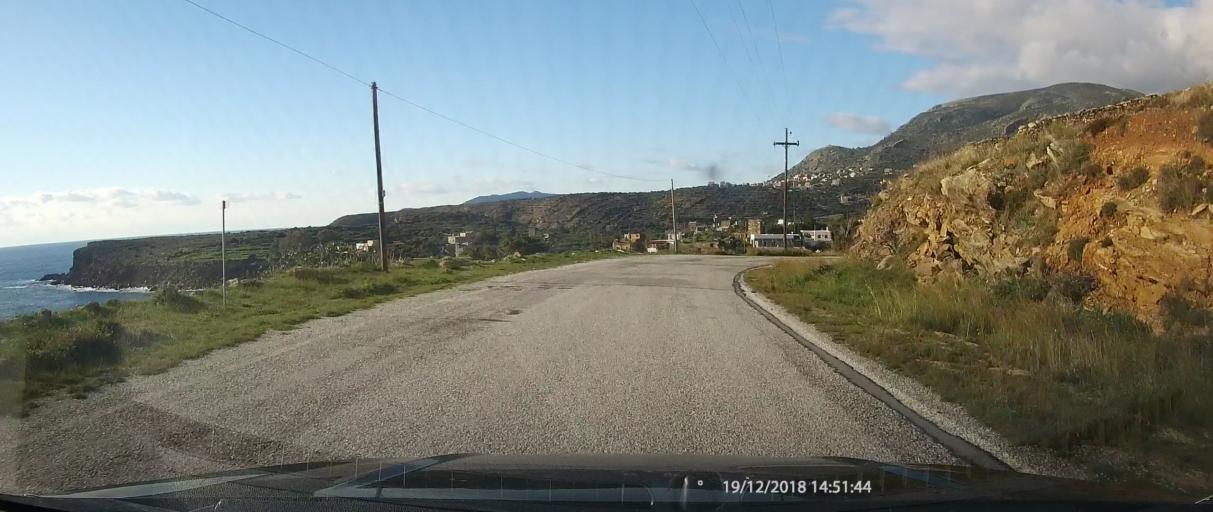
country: GR
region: Peloponnese
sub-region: Nomos Lakonias
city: Gytheio
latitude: 36.4595
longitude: 22.4450
